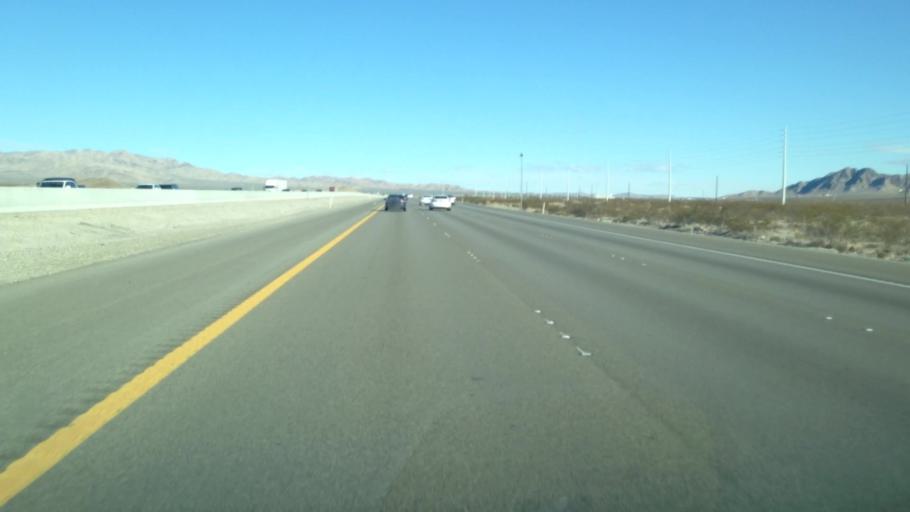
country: US
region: Nevada
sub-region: Clark County
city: Sandy Valley
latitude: 35.7260
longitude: -115.3612
